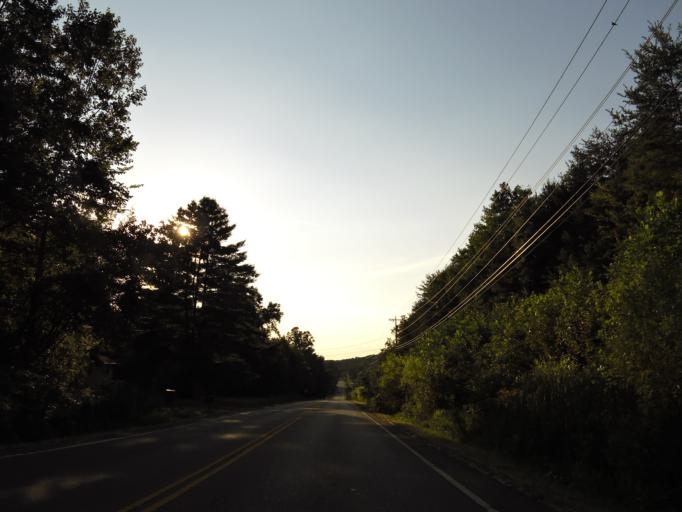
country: US
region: Tennessee
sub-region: McMinn County
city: Athens
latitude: 35.4268
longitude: -84.5689
